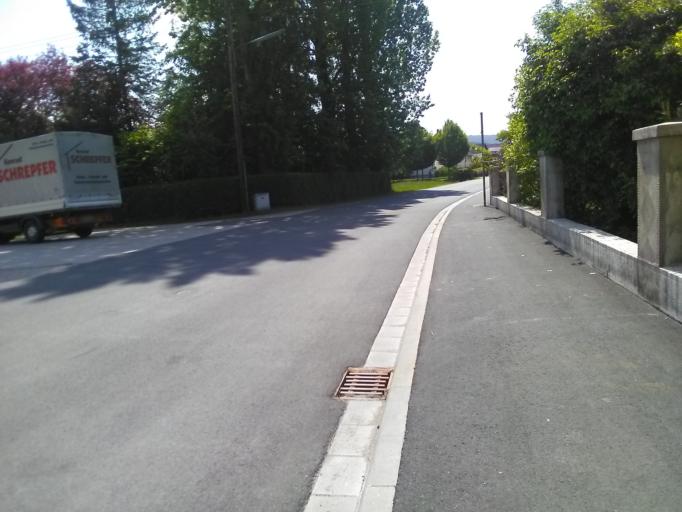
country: DE
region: Bavaria
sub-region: Upper Franconia
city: Kronach
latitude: 50.2162
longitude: 11.3069
